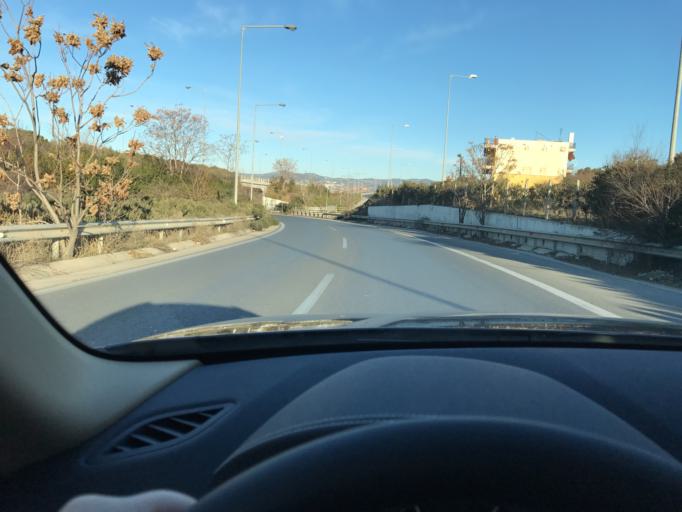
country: GR
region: Central Macedonia
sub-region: Nomos Thessalonikis
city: Efkarpia
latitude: 40.6778
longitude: 22.9595
